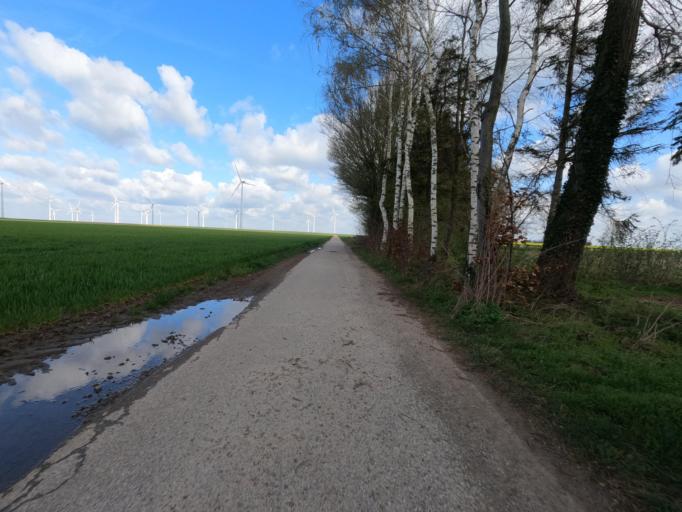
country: DE
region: North Rhine-Westphalia
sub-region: Regierungsbezirk Koln
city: Linnich
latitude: 51.0042
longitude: 6.3172
